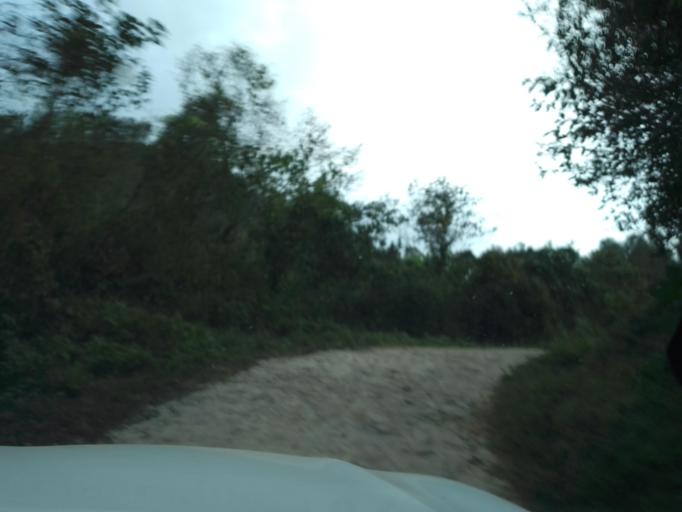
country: MX
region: Chiapas
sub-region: Cacahoatan
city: Benito Juarez
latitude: 15.2077
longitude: -92.2212
